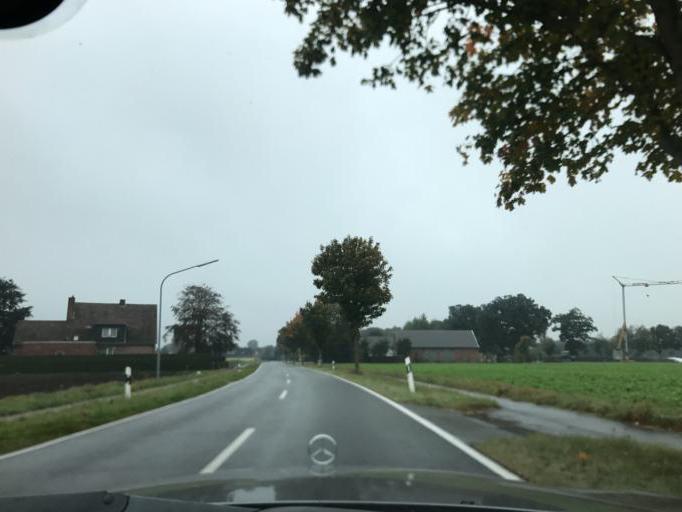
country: DE
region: Lower Saxony
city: Papenburg
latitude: 53.0750
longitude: 7.3459
